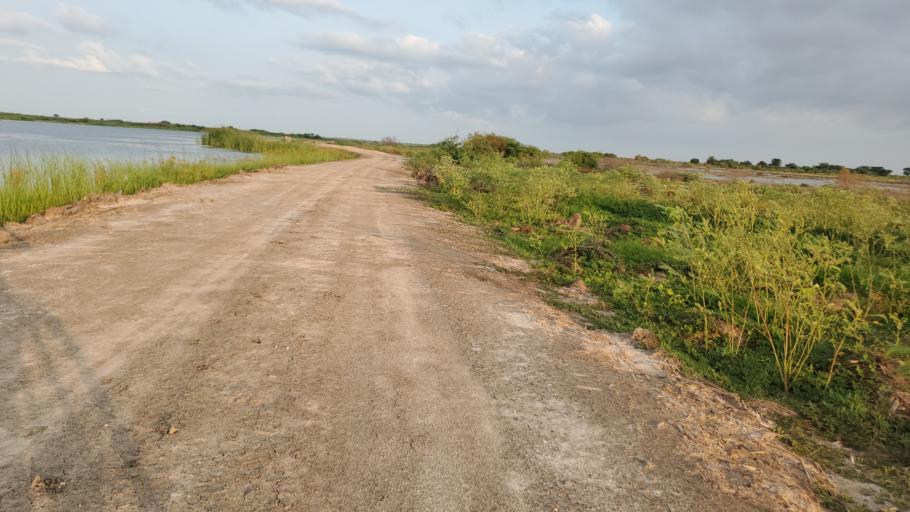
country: SN
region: Saint-Louis
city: Saint-Louis
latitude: 16.0191
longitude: -16.4052
